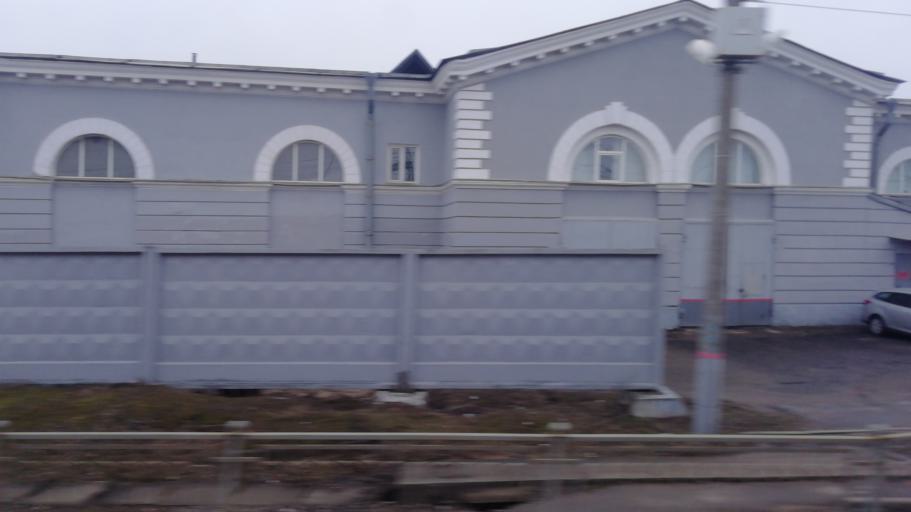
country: RU
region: St.-Petersburg
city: Kupchino
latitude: 59.8880
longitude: 30.3453
